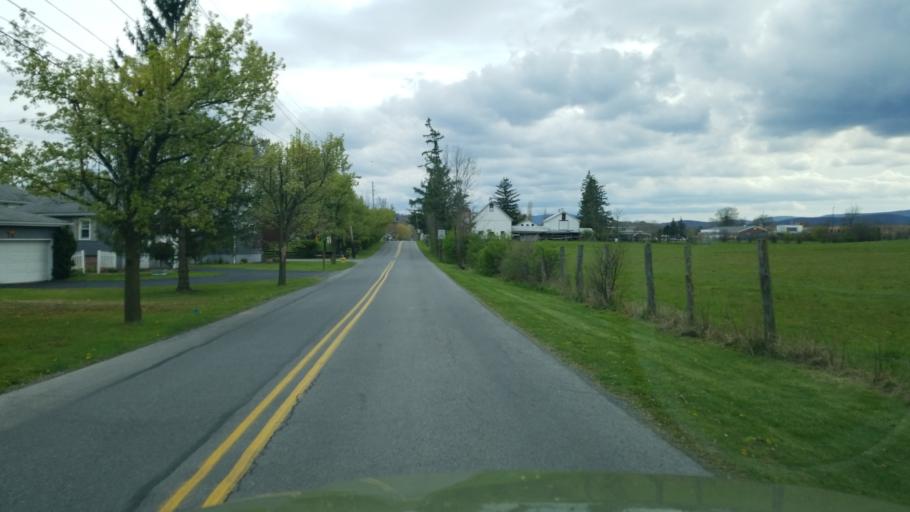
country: US
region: Pennsylvania
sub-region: Blair County
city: Hollidaysburg
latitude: 40.4383
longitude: -78.4025
